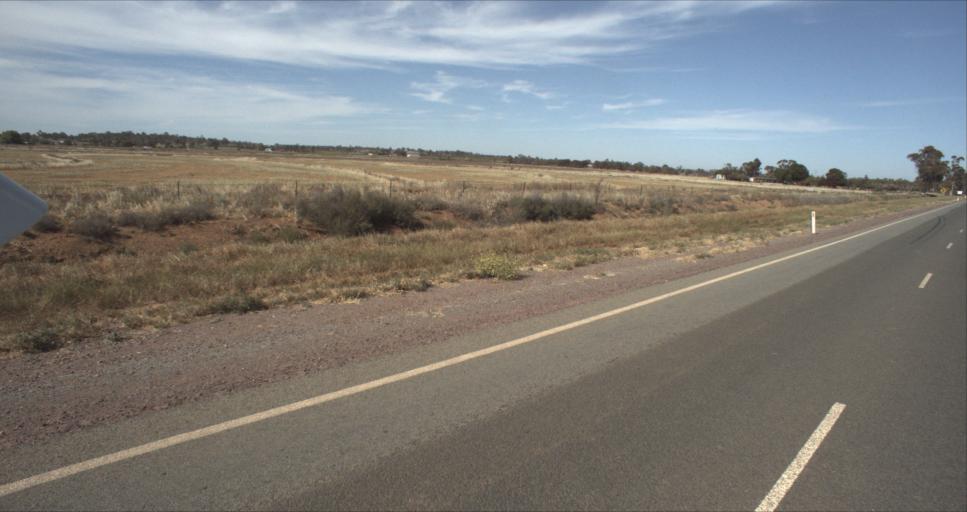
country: AU
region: New South Wales
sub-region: Leeton
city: Leeton
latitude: -34.5581
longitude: 146.4445
